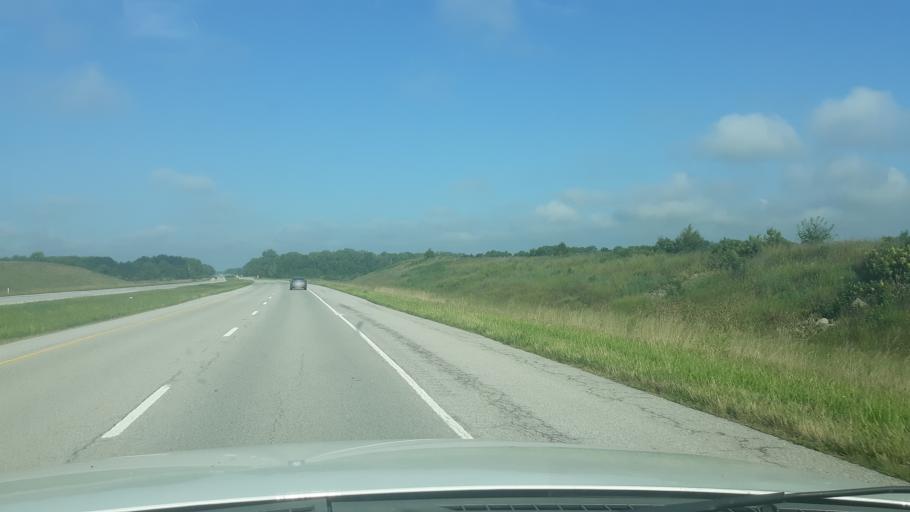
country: US
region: Illinois
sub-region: Saline County
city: Carrier Mills
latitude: 37.7332
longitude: -88.6174
